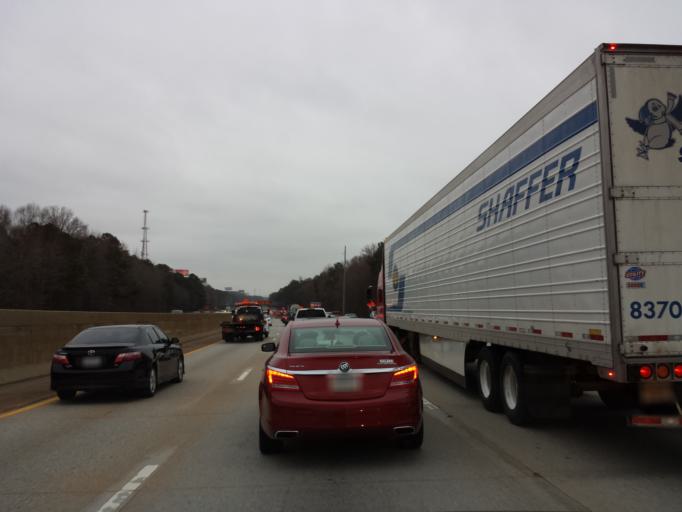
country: US
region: Georgia
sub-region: Clayton County
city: Morrow
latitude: 33.5570
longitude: -84.3067
